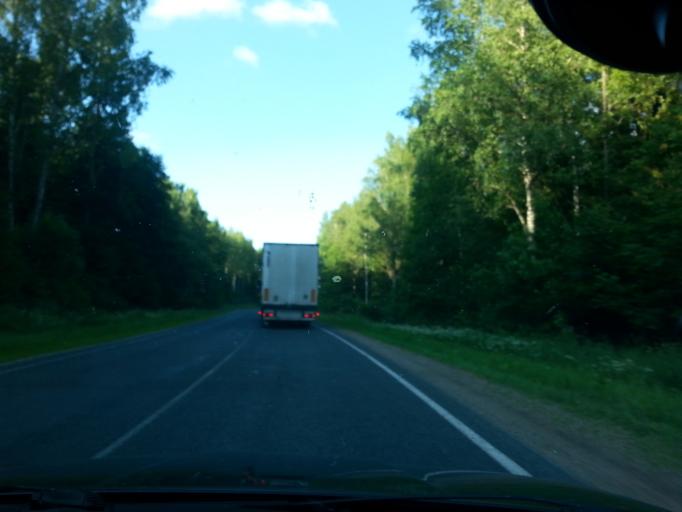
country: BY
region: Minsk
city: Svir
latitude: 54.8559
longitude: 26.3105
